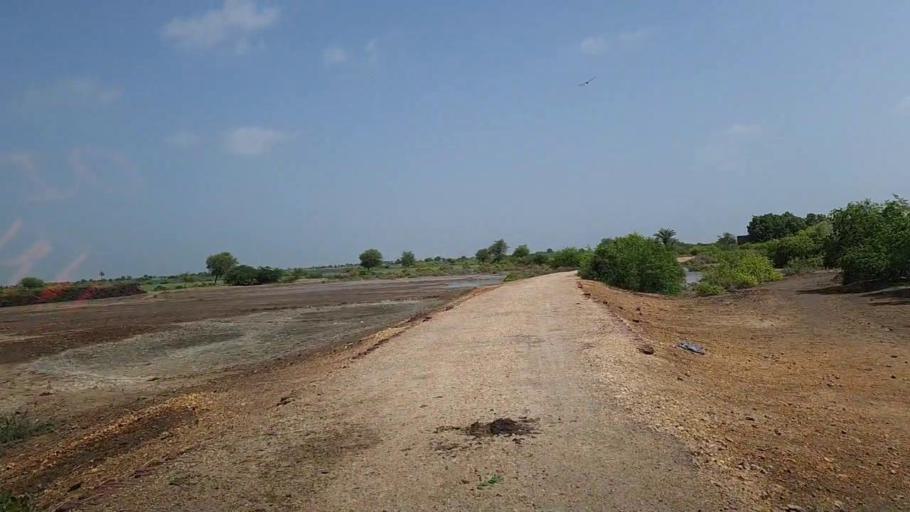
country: PK
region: Sindh
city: Mirpur Batoro
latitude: 24.6501
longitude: 68.4261
